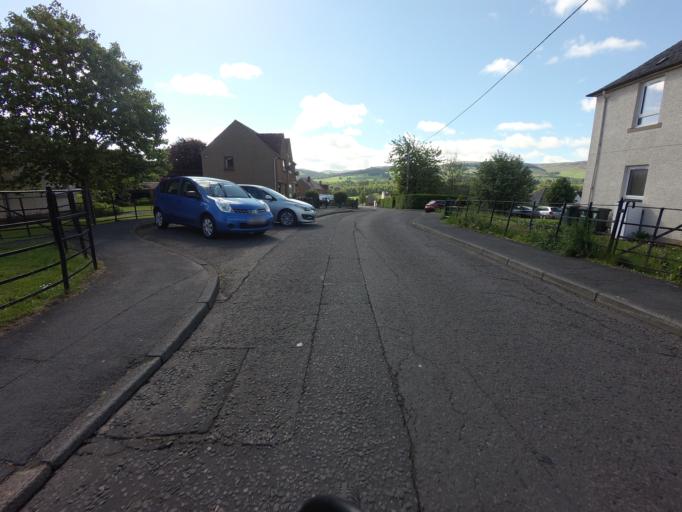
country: GB
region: Scotland
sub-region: Perth and Kinross
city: Auchterarder
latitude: 56.2940
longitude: -3.7100
